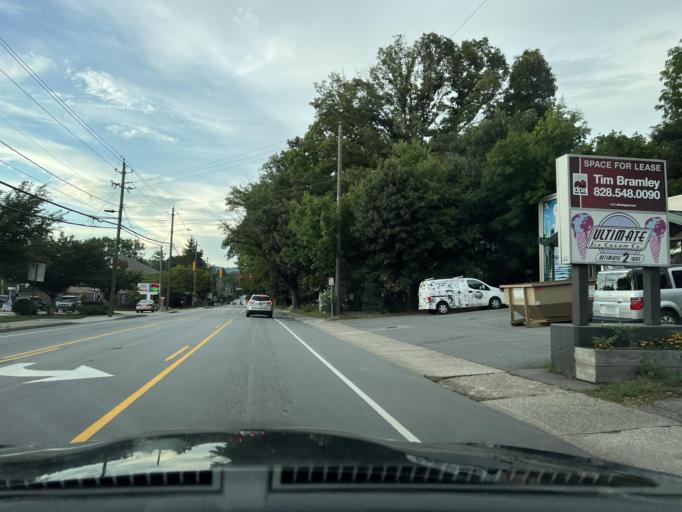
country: US
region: North Carolina
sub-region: Buncombe County
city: Asheville
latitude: 35.6063
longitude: -82.5463
